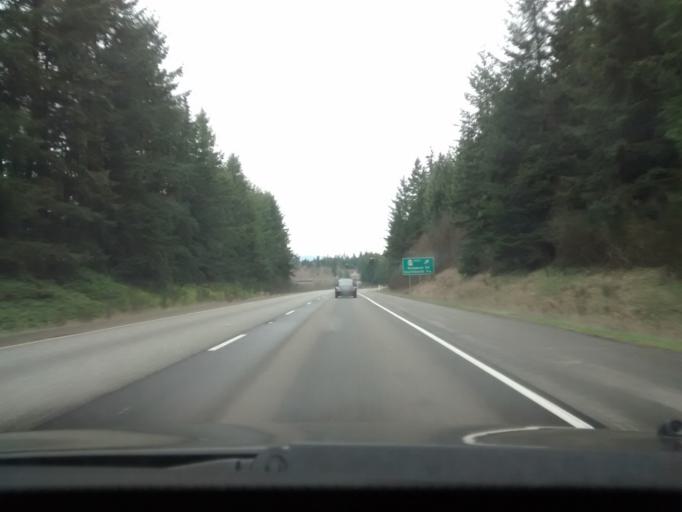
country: US
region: Washington
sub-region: Kitsap County
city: Bethel
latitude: 47.4971
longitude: -122.6415
